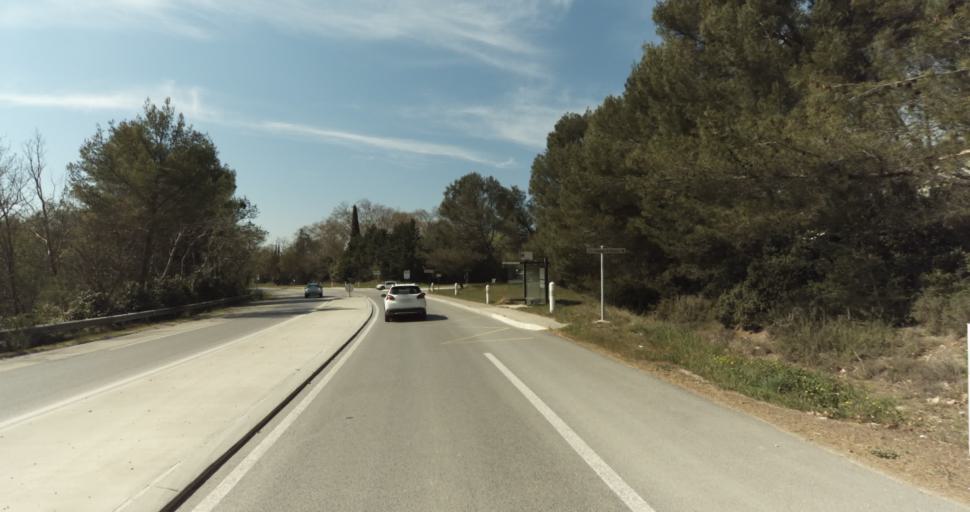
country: FR
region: Provence-Alpes-Cote d'Azur
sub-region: Departement des Bouches-du-Rhone
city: Ventabren
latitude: 43.5492
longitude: 5.3019
